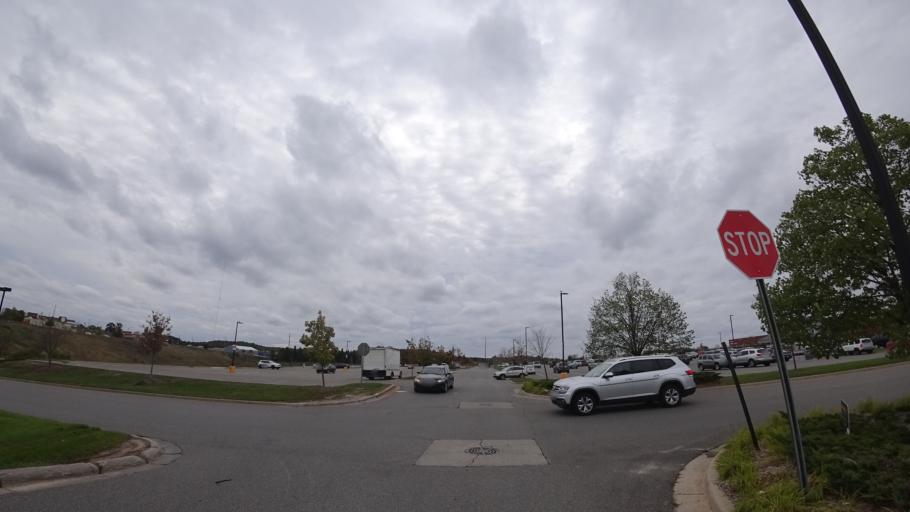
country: US
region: Michigan
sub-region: Emmet County
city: Petoskey
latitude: 45.3511
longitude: -84.9718
